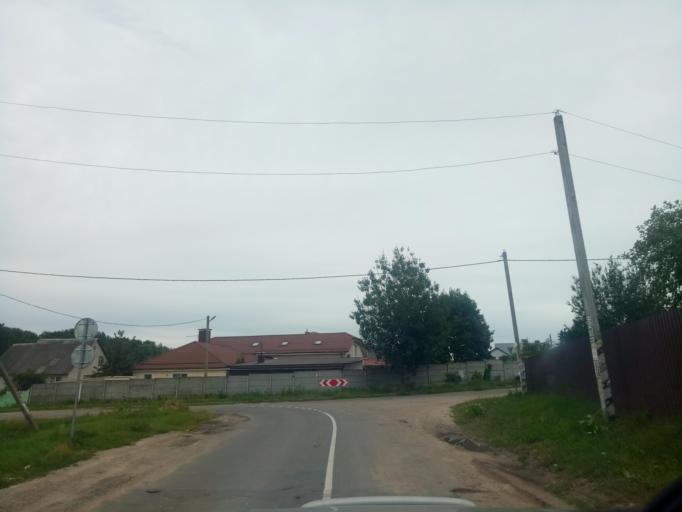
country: BY
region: Minsk
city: Zhdanovichy
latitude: 53.9246
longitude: 27.3839
